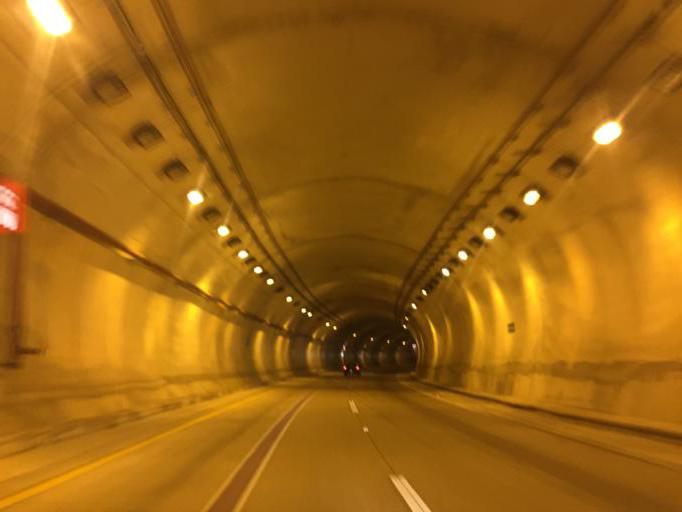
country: MX
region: Puebla
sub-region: Xicotepec
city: San Lorenzo
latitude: 20.3242
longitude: -97.9656
